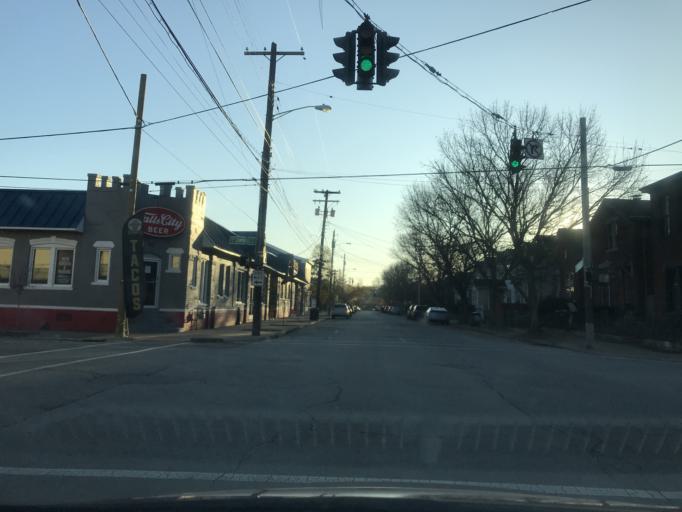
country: US
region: Kentucky
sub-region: Jefferson County
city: Louisville
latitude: 38.2503
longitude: -85.7366
